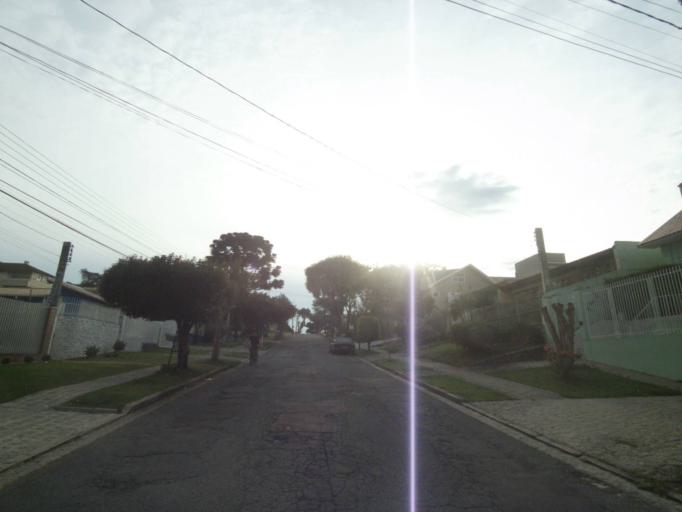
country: BR
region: Parana
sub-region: Curitiba
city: Curitiba
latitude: -25.4296
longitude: -49.2375
